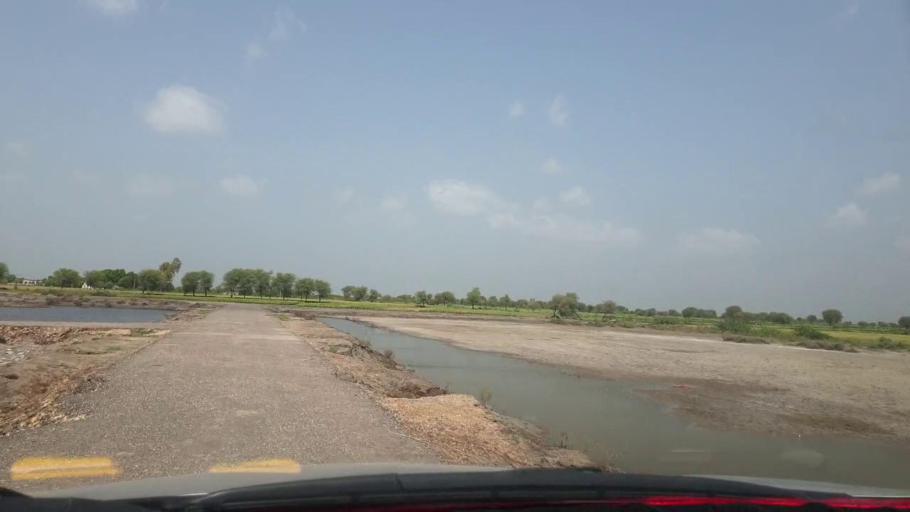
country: PK
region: Sindh
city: Rajo Khanani
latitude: 24.9283
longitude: 68.9006
